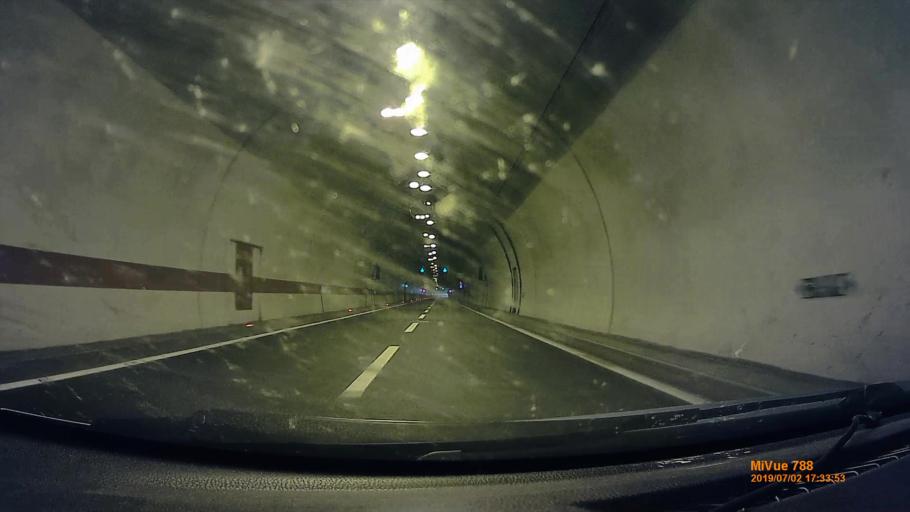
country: HR
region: Primorsko-Goranska
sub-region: Grad Delnice
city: Delnice
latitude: 45.3832
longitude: 14.8022
